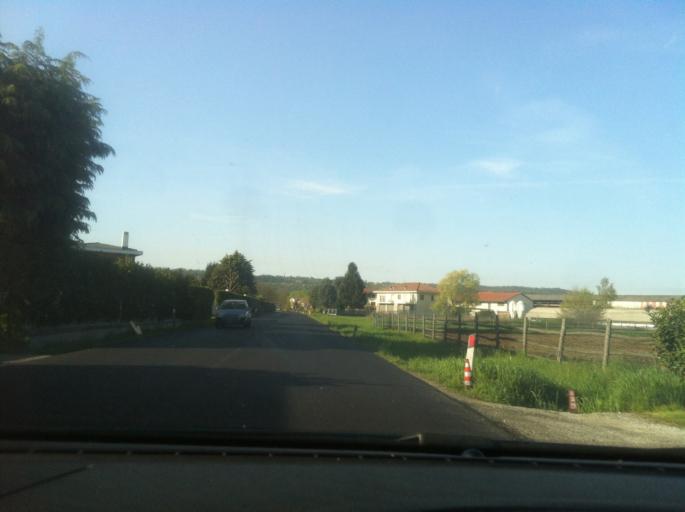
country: IT
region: Piedmont
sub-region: Provincia di Torino
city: Mercenasco
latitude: 45.3710
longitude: 7.8787
